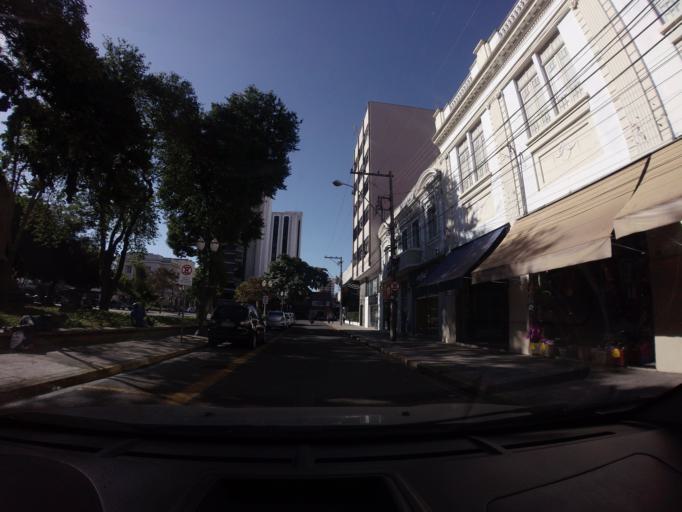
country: BR
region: Sao Paulo
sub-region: Piracicaba
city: Piracicaba
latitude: -22.7242
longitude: -47.6482
